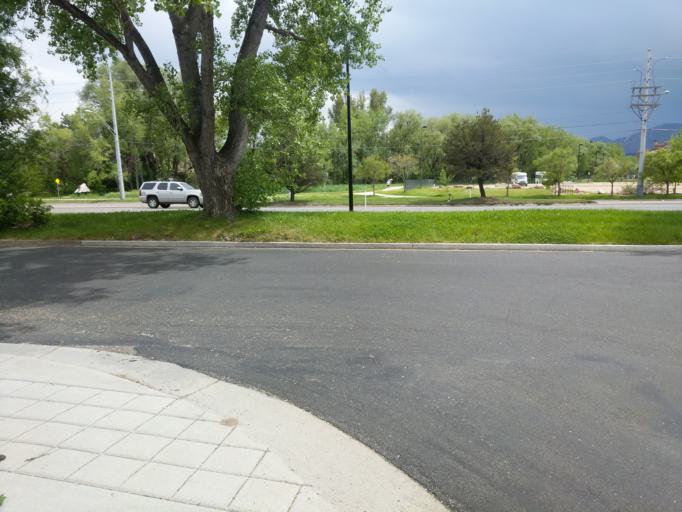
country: US
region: Colorado
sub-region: Boulder County
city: Boulder
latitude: 40.0004
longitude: -105.2475
